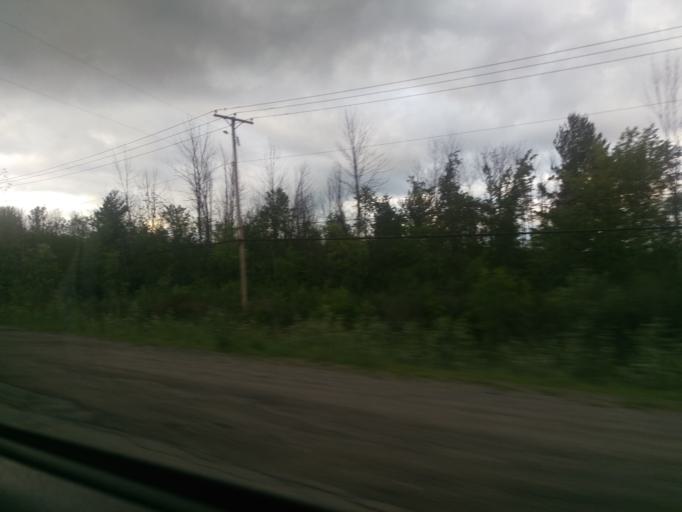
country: CA
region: Quebec
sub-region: Outaouais
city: Gatineau
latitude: 45.4811
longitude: -75.7472
